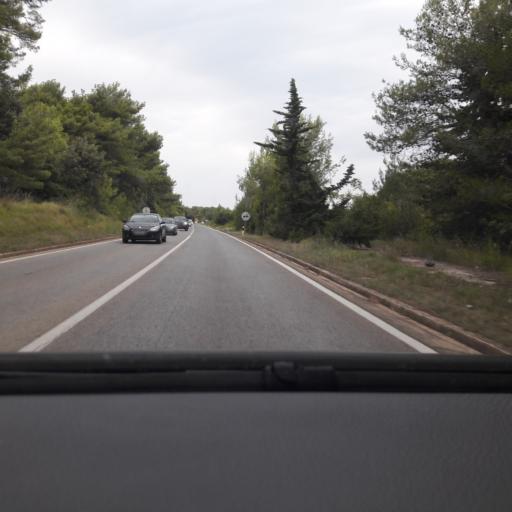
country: HR
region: Zadarska
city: Zadar
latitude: 44.1490
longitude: 15.2221
